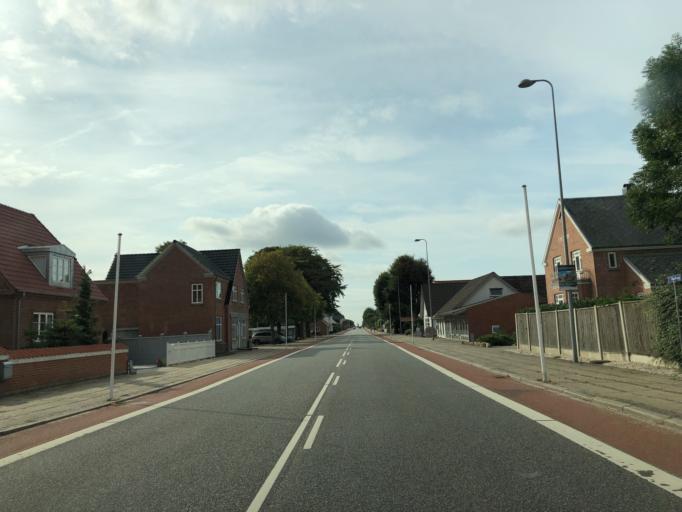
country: DK
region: Central Jutland
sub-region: Ringkobing-Skjern Kommune
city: Skjern
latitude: 55.9437
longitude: 8.4973
